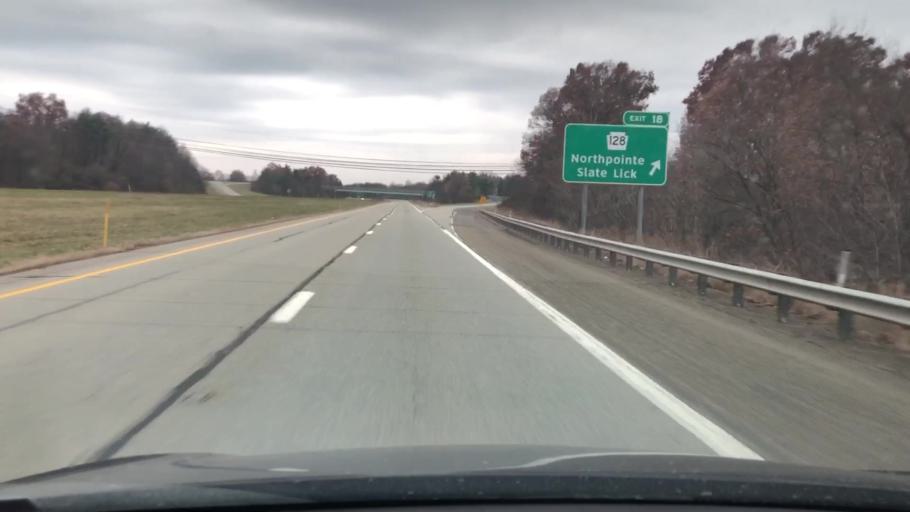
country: US
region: Pennsylvania
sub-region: Armstrong County
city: Freeport
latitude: 40.7591
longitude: -79.6367
